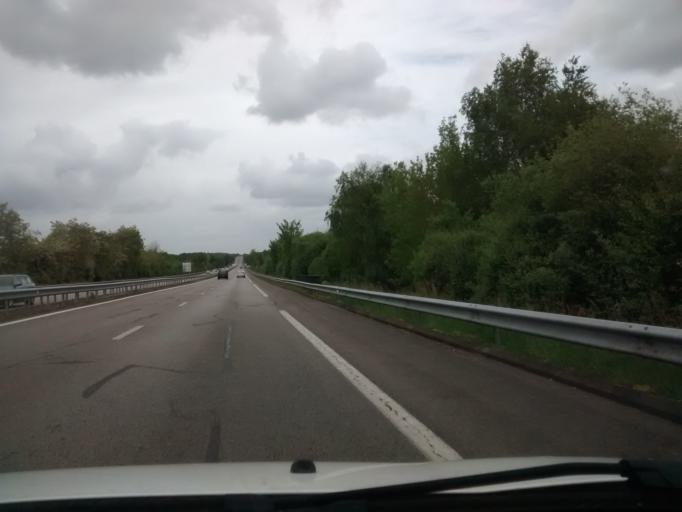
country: FR
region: Brittany
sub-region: Departement du Morbihan
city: Malestroit
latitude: 47.8323
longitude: -2.4303
